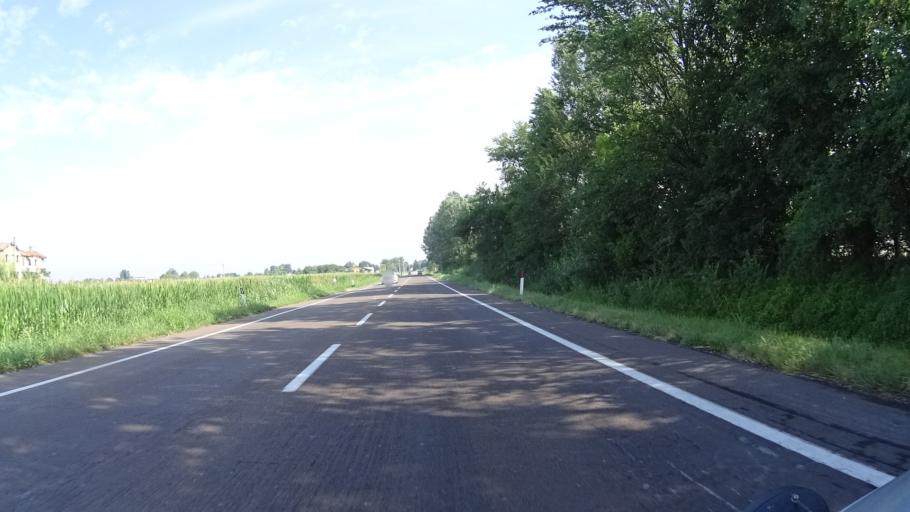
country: IT
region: Veneto
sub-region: Provincia di Venezia
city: San Michele al Tagliamento
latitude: 45.7630
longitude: 12.9855
